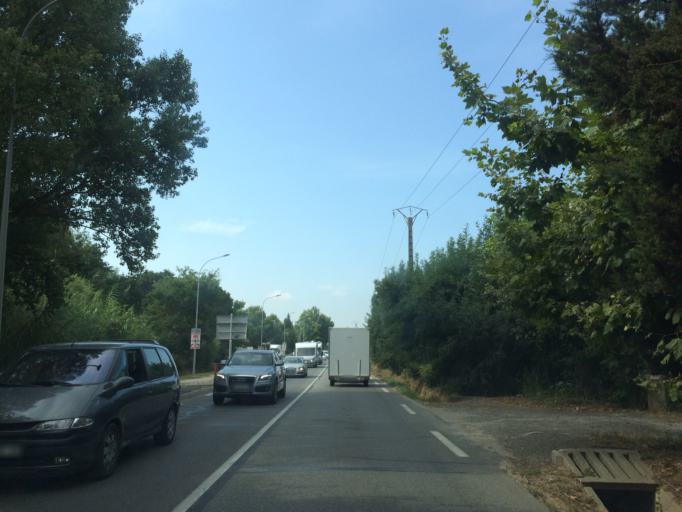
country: FR
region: Provence-Alpes-Cote d'Azur
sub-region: Departement du Var
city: Gassin
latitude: 43.2778
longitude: 6.5759
